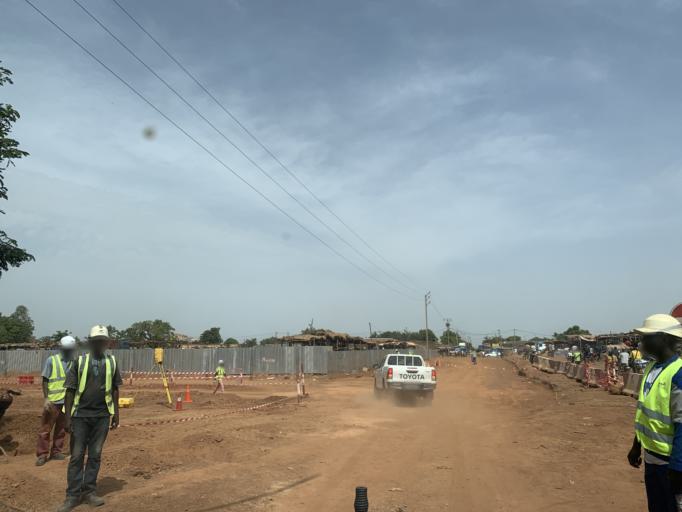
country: BF
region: Centre
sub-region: Kadiogo Province
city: Ouagadougou
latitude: 12.3359
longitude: -1.5155
